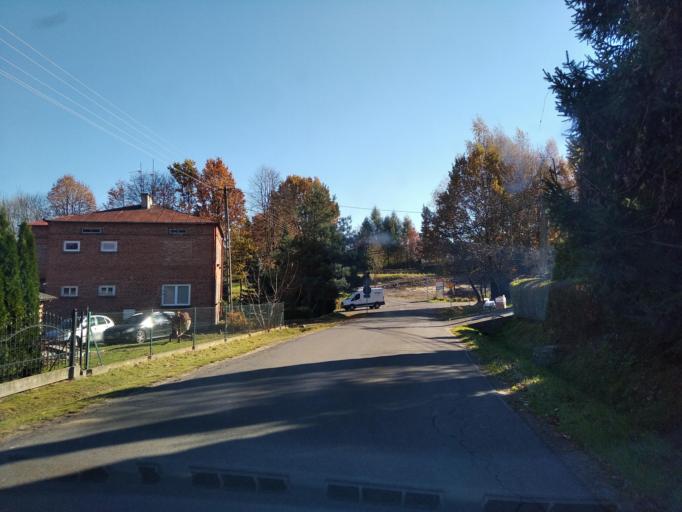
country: PL
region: Subcarpathian Voivodeship
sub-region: Powiat rzeszowski
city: Siedliska
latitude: 49.9645
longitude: 21.9841
